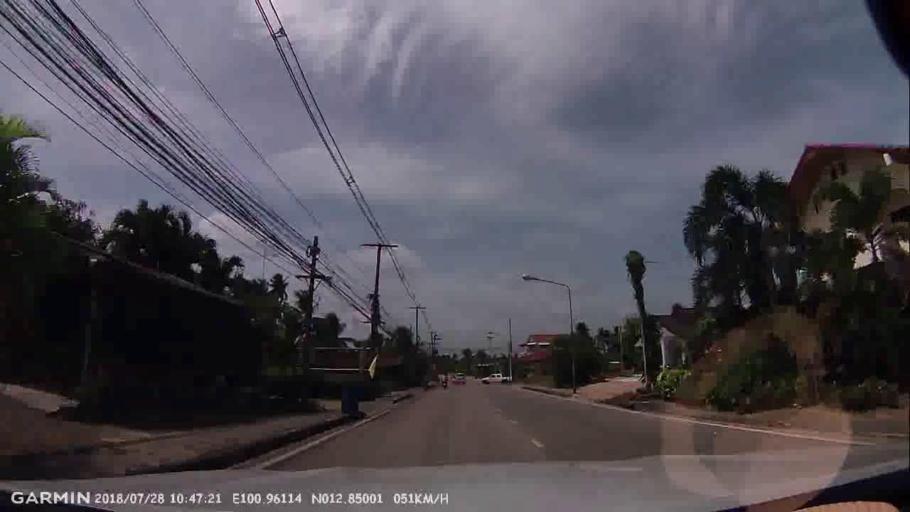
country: TH
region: Chon Buri
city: Phatthaya
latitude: 12.8499
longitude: 100.9611
